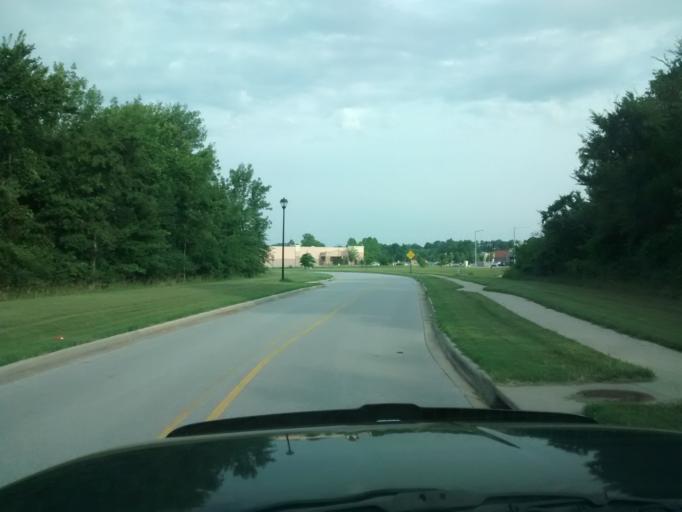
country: US
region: Arkansas
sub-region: Washington County
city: Fayetteville
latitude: 36.0752
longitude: -94.2073
